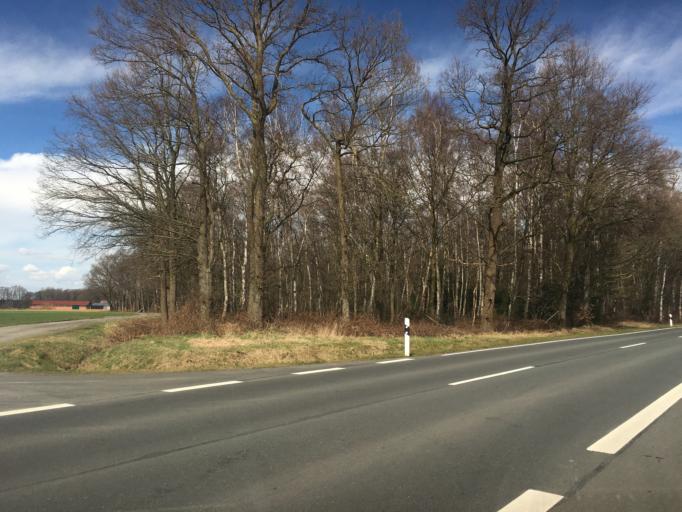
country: DE
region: North Rhine-Westphalia
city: Olfen
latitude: 51.7427
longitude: 7.4017
